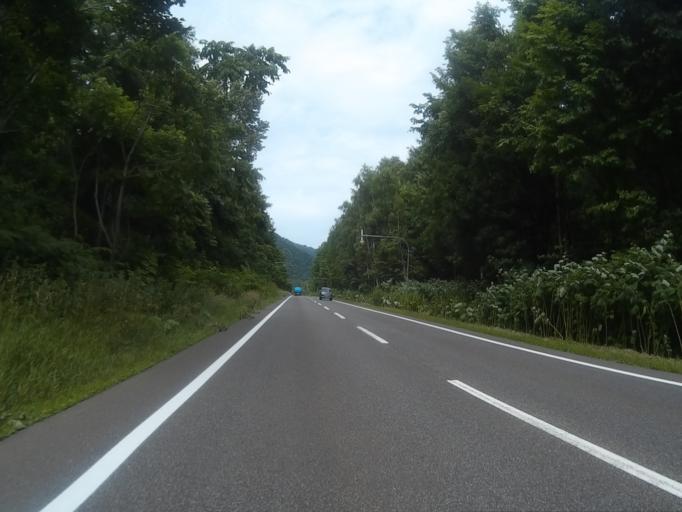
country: JP
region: Hokkaido
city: Sapporo
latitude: 42.9317
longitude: 141.1199
